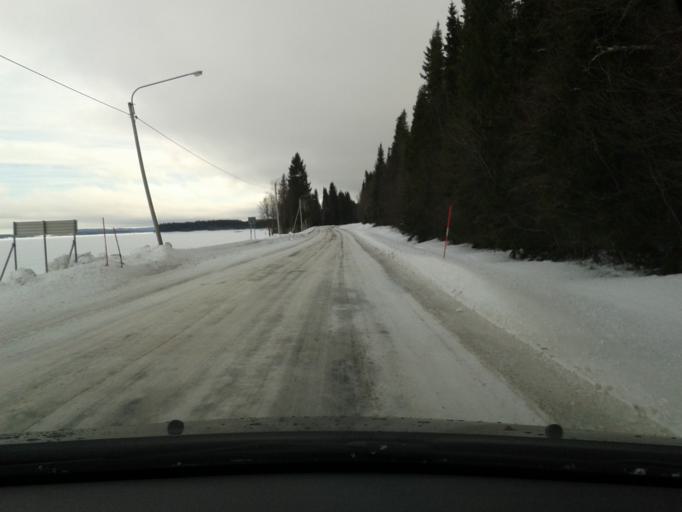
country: SE
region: Vaesterbotten
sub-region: Vilhelmina Kommun
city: Sjoberg
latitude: 64.6652
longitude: 16.3057
